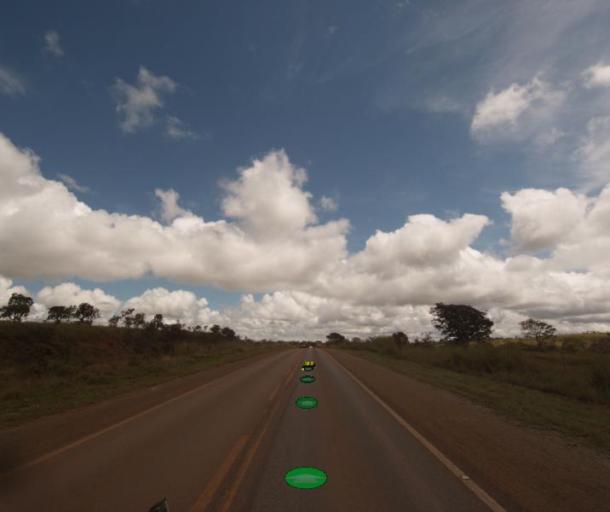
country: BR
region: Goias
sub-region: Pirenopolis
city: Pirenopolis
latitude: -15.7764
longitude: -48.5208
